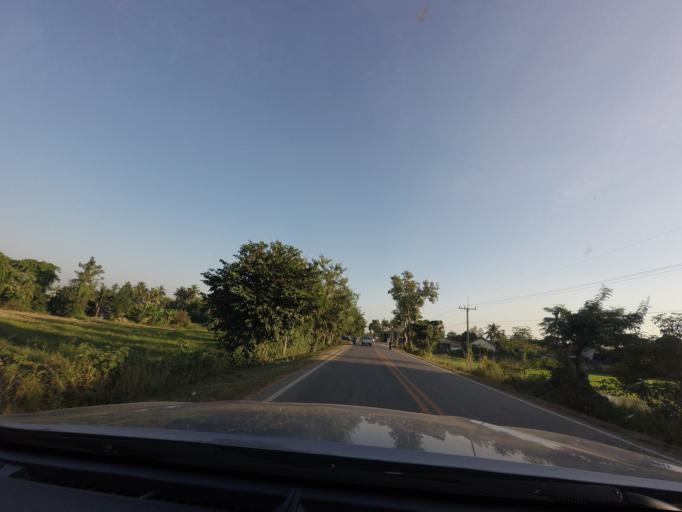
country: TH
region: Sukhothai
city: Sawankhalok
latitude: 17.3704
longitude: 99.8021
